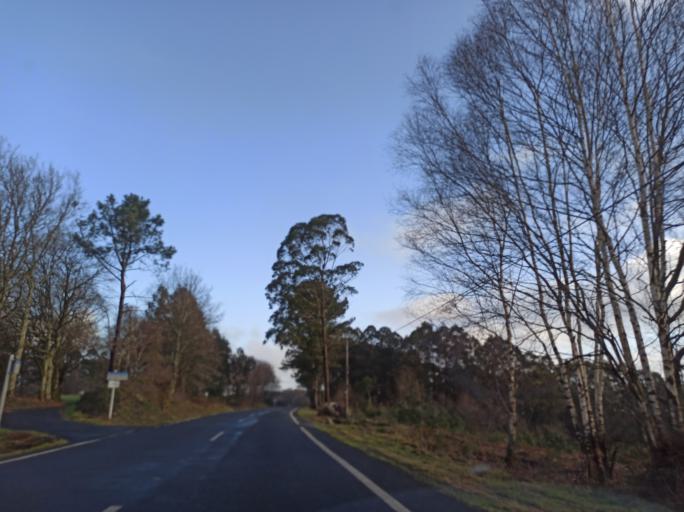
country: ES
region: Galicia
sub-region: Provincia da Coruna
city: Sobrado
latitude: 43.0875
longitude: -7.9983
